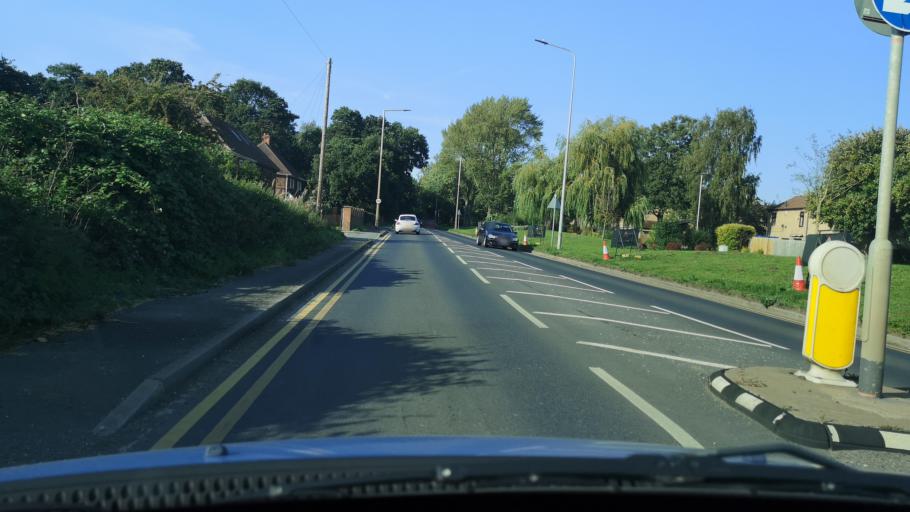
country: GB
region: England
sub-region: North Lincolnshire
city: Scunthorpe
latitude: 53.5746
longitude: -0.6832
